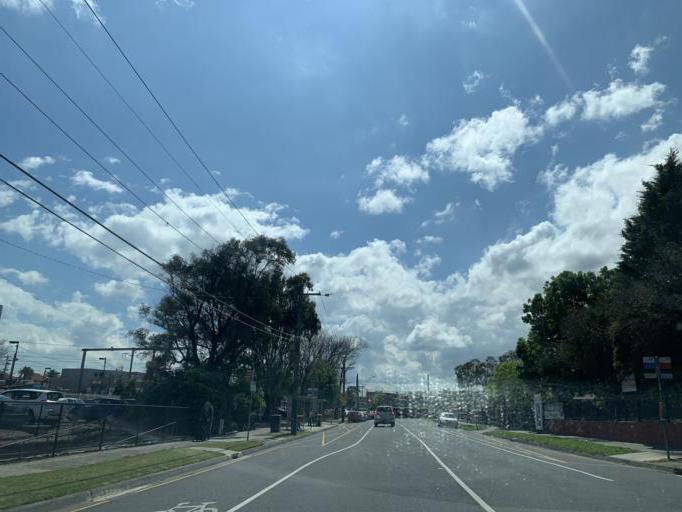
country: AU
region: Victoria
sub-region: Kingston
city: Mordialloc
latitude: -38.0062
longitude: 145.0879
